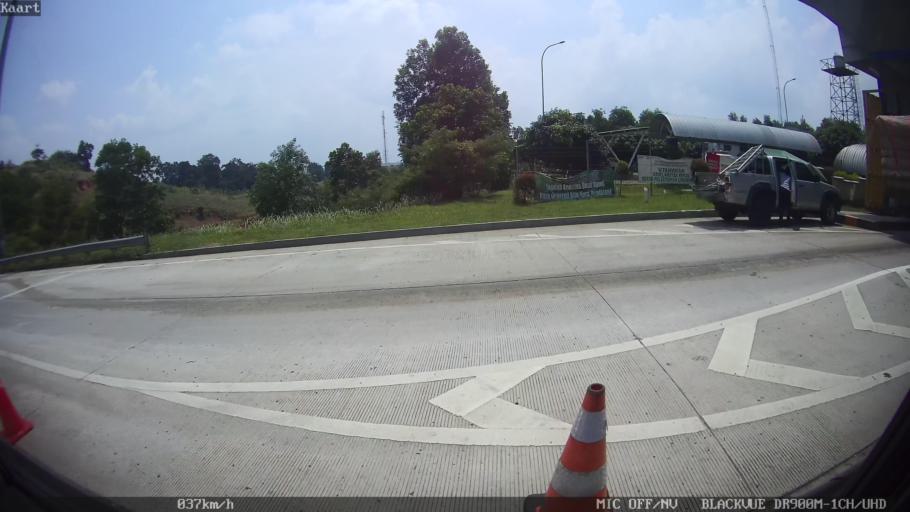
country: ID
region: Lampung
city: Panjang
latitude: -5.4050
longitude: 105.3467
